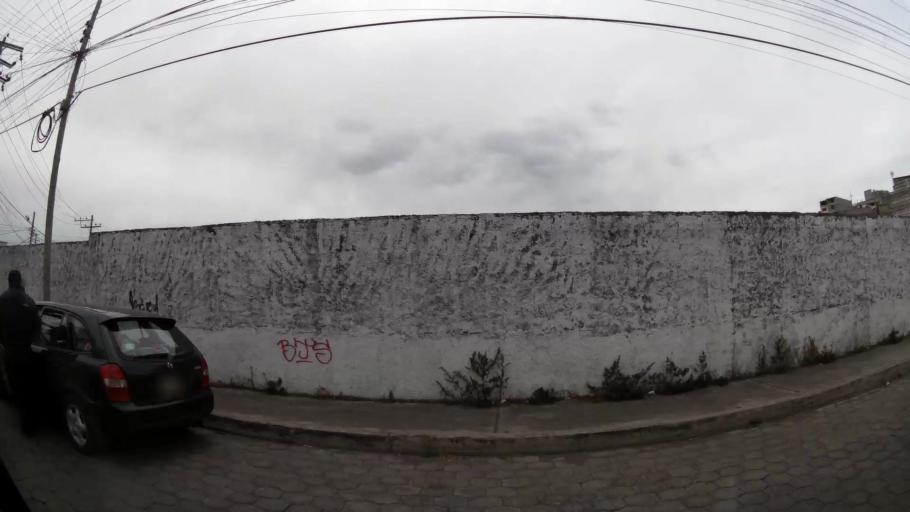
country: EC
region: Cotopaxi
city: Latacunga
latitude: -0.9344
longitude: -78.6103
